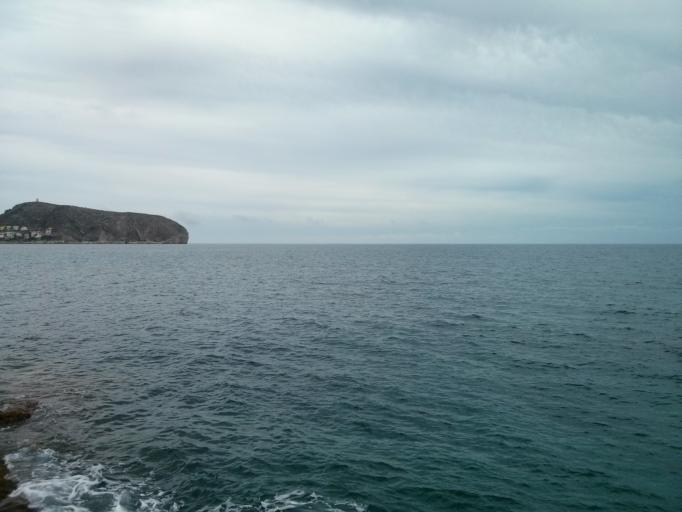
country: ES
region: Valencia
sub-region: Provincia de Alicante
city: Moraira
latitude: 38.6810
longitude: 0.1210
